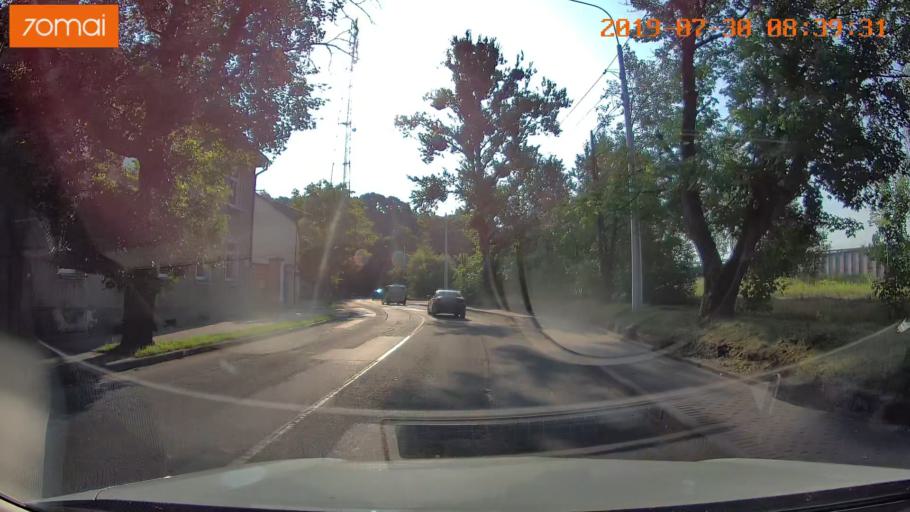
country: RU
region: Kaliningrad
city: Chernyakhovsk
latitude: 54.6310
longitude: 21.8043
